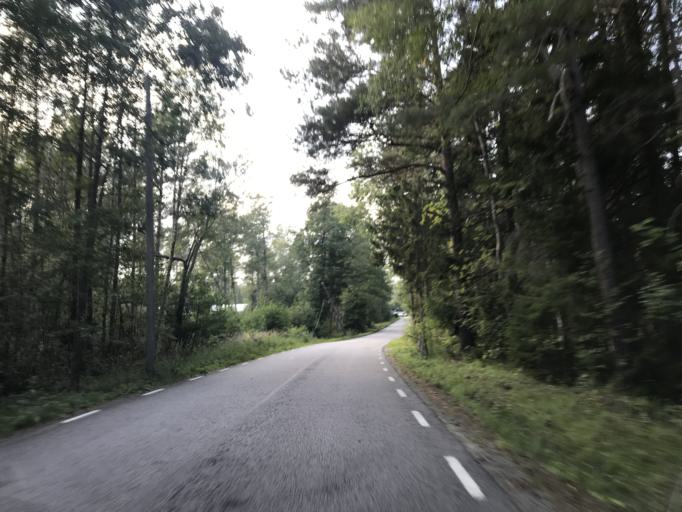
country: SE
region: Stockholm
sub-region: Norrtalje Kommun
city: Bjorko
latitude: 59.8670
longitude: 19.0279
